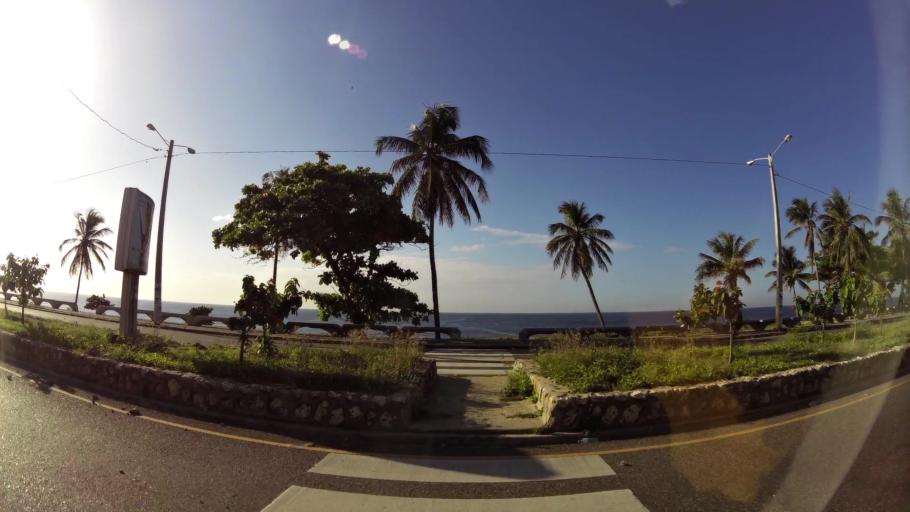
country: DO
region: Santo Domingo
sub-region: Santo Domingo
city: Santo Domingo Este
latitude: 18.4688
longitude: -69.8357
